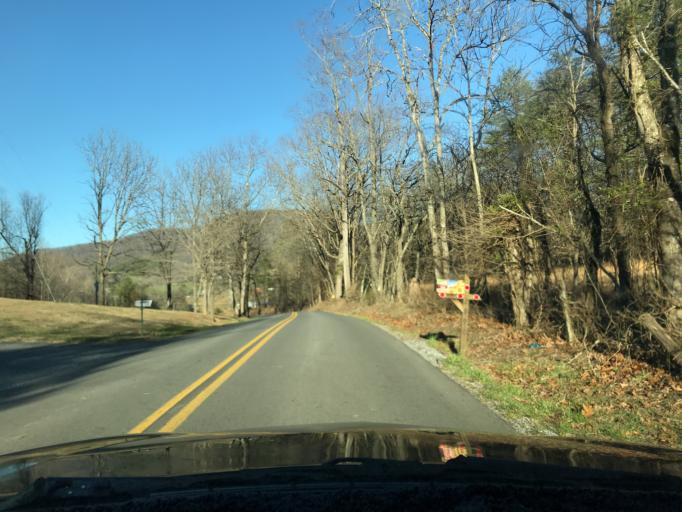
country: US
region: Virginia
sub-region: Botetourt County
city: Blue Ridge
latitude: 37.3967
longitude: -79.7070
